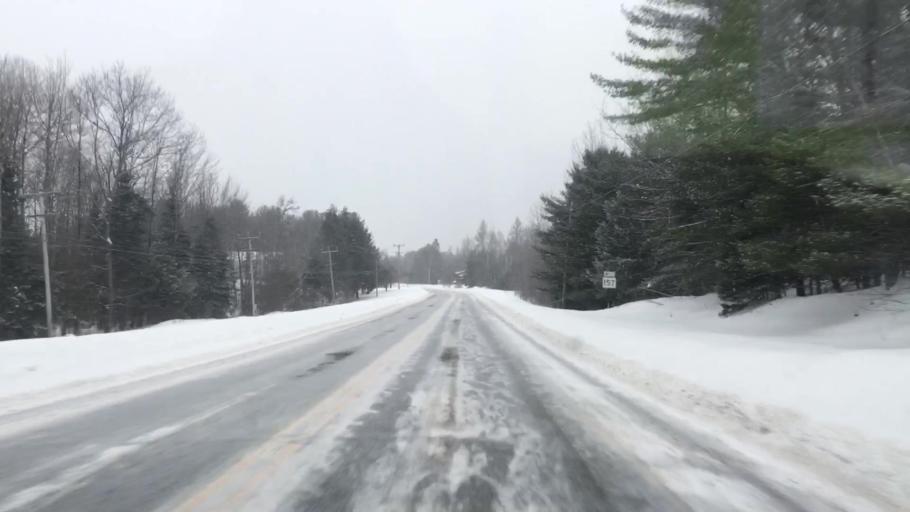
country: US
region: Maine
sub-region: Penobscot County
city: Medway
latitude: 45.5415
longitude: -68.3692
